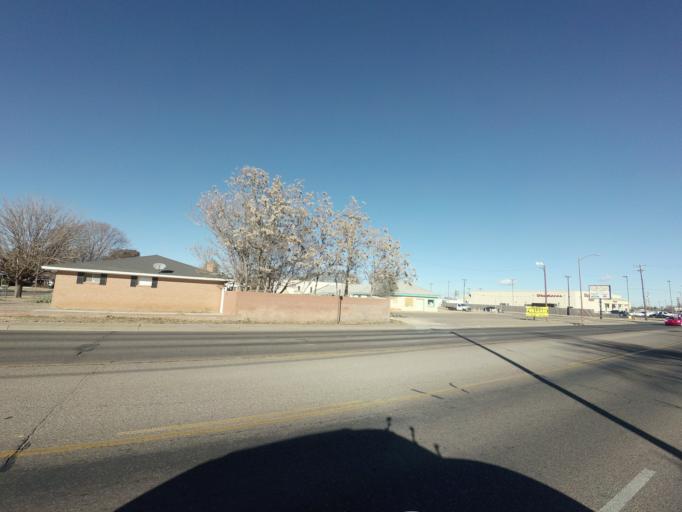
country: US
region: New Mexico
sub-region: Curry County
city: Clovis
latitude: 34.4193
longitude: -103.1986
